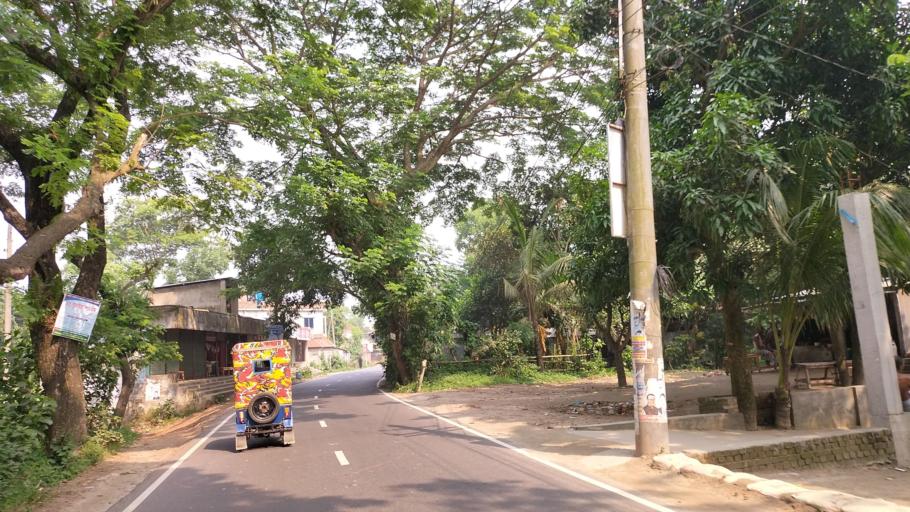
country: BD
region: Dhaka
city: Azimpur
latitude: 23.6956
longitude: 90.2988
